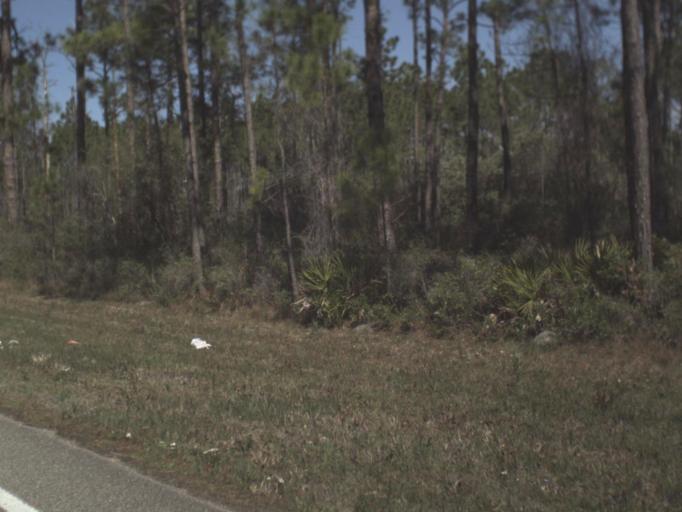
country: US
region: Florida
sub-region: Gulf County
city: Port Saint Joe
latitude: 29.7571
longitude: -85.2558
